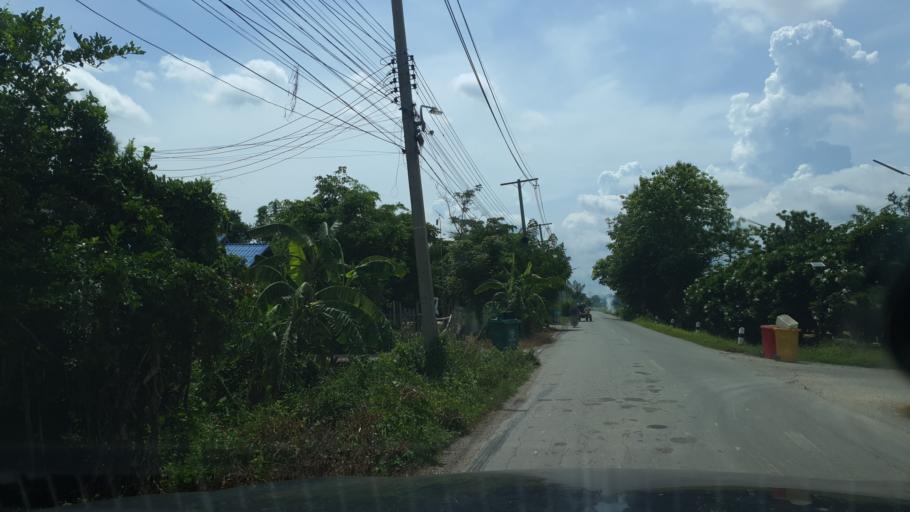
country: TH
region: Sukhothai
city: Sukhothai
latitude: 16.9960
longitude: 99.8570
